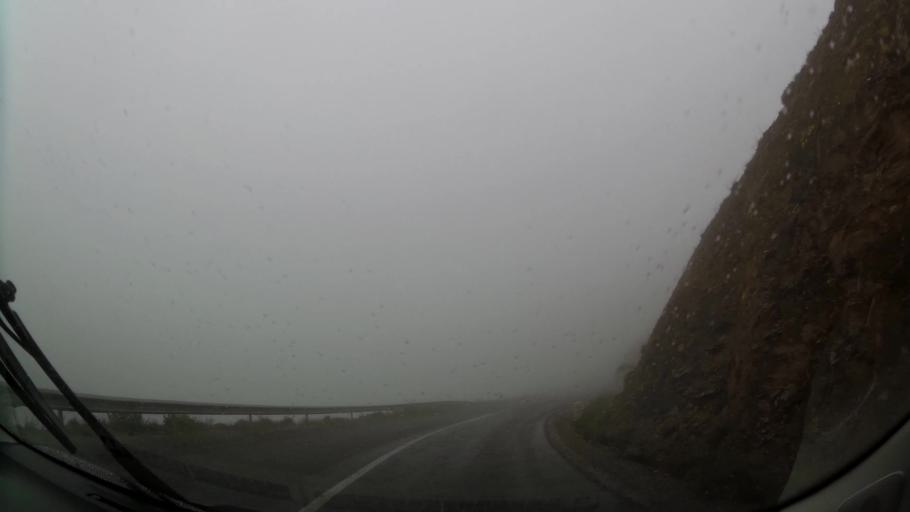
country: MA
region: Oriental
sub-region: Nador
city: Boudinar
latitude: 35.1034
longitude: -3.5551
